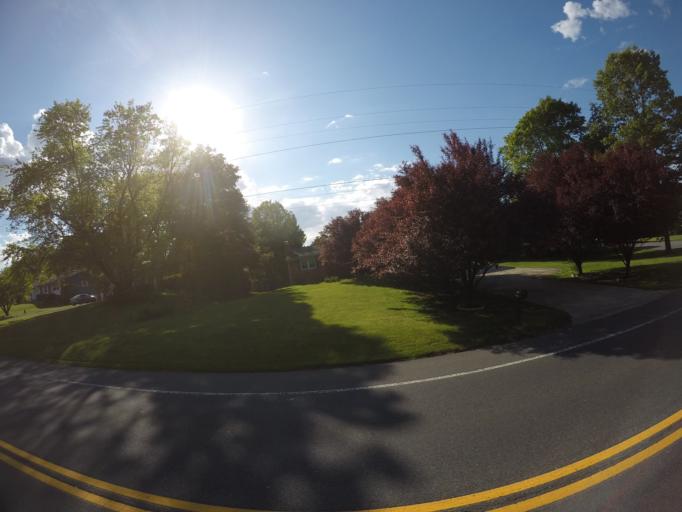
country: US
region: Maryland
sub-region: Montgomery County
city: Damascus
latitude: 39.3311
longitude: -77.1867
